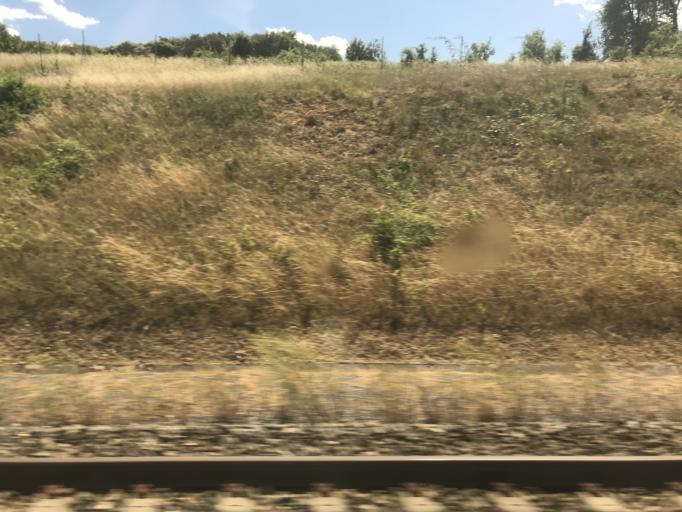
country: FR
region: Lorraine
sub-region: Departement de Meurthe-et-Moselle
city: Pagny-sur-Moselle
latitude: 48.9709
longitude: 5.9557
